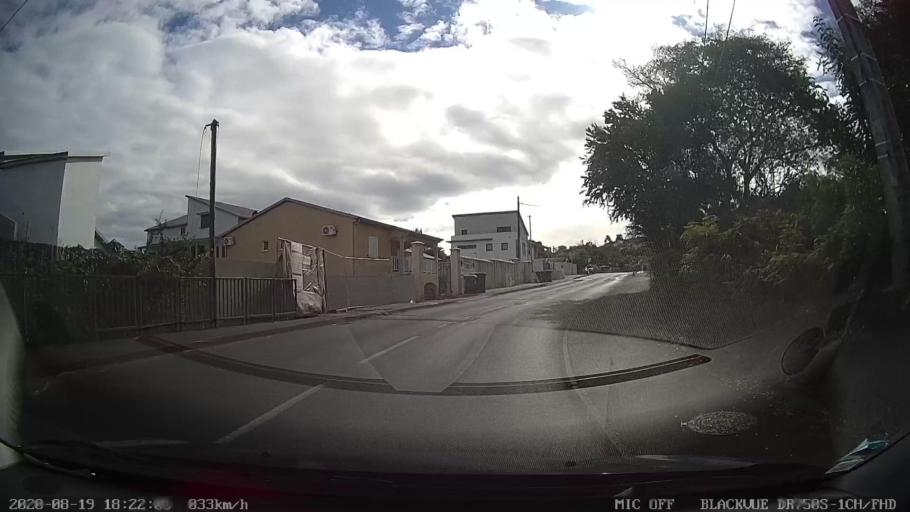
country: RE
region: Reunion
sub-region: Reunion
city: La Possession
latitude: -20.9556
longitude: 55.3373
